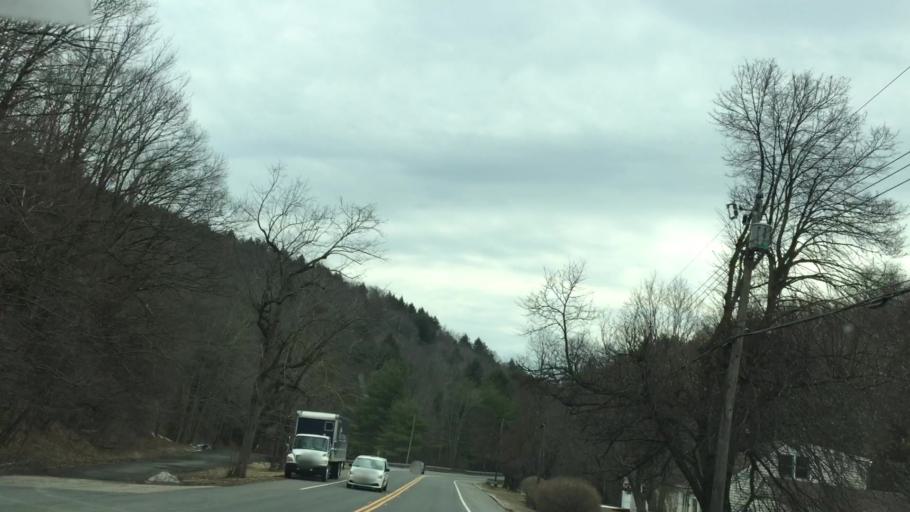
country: US
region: Massachusetts
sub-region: Berkshire County
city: Lanesborough
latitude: 42.6134
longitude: -73.2320
